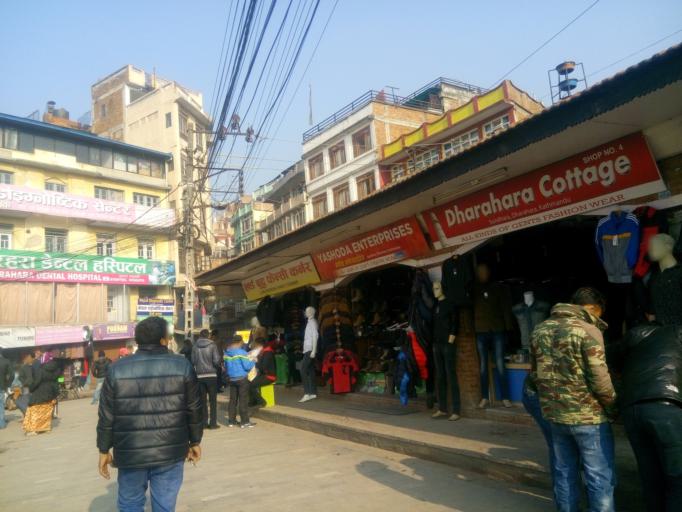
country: NP
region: Central Region
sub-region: Bagmati Zone
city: Kathmandu
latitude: 27.7005
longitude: 85.3121
